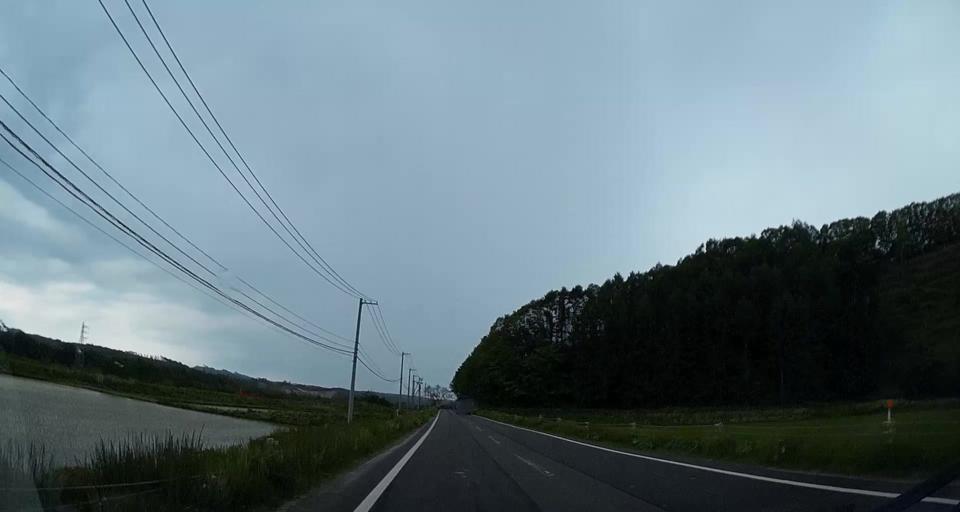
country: JP
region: Hokkaido
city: Chitose
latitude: 42.7559
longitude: 141.9162
